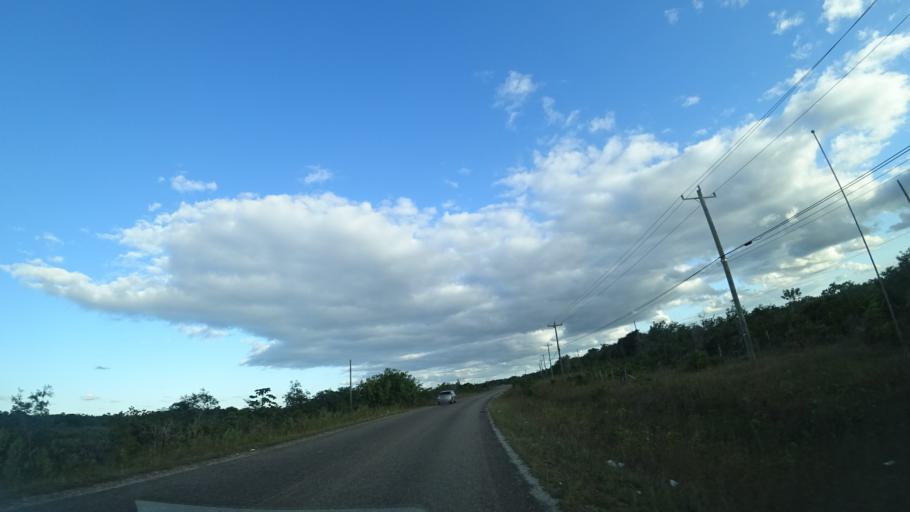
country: BZ
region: Belize
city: Belize City
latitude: 17.5811
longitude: -88.3737
